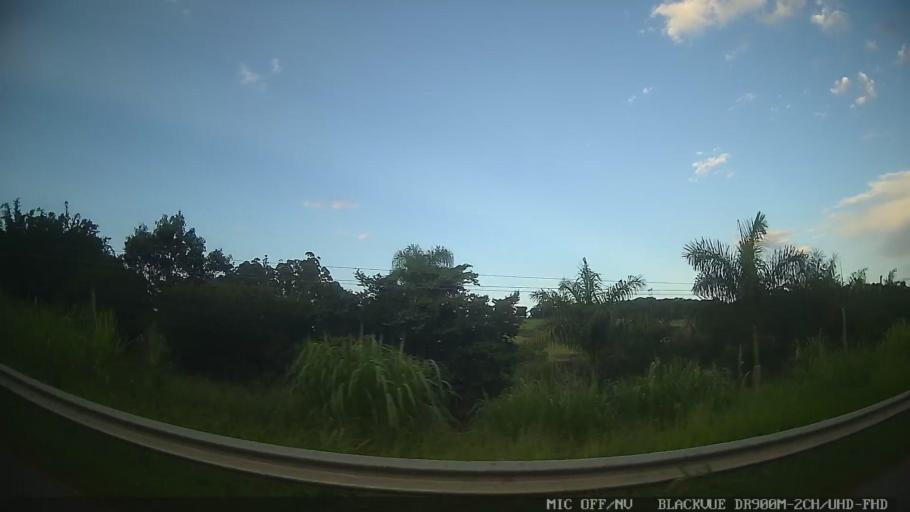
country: BR
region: Sao Paulo
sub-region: Braganca Paulista
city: Braganca Paulista
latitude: -22.9455
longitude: -46.6267
